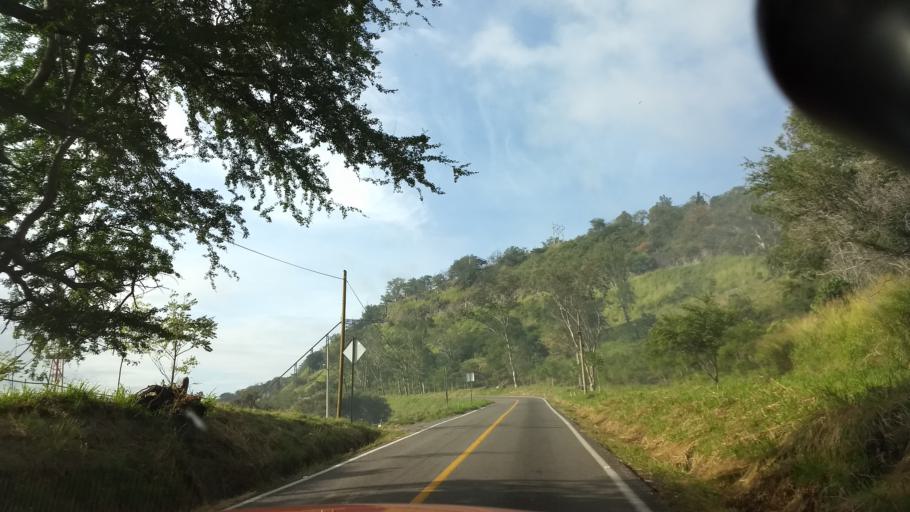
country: MX
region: Jalisco
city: Tuxpan
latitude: 19.5273
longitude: -103.4386
